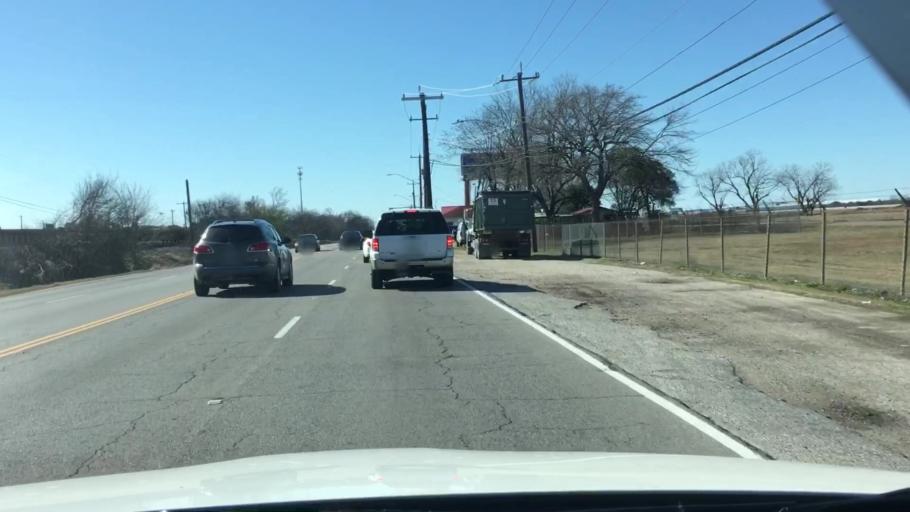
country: US
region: Texas
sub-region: Bexar County
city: Alamo Heights
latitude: 29.5414
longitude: -98.4434
